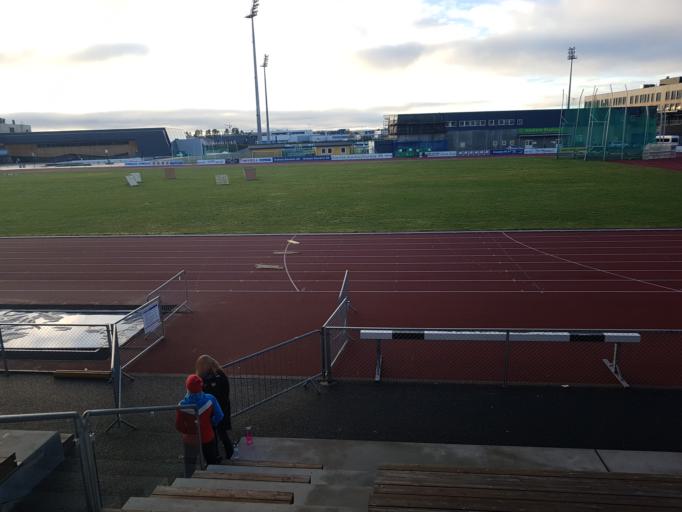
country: NO
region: Akershus
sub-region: Ullensaker
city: Jessheim
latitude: 60.1498
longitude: 11.1929
